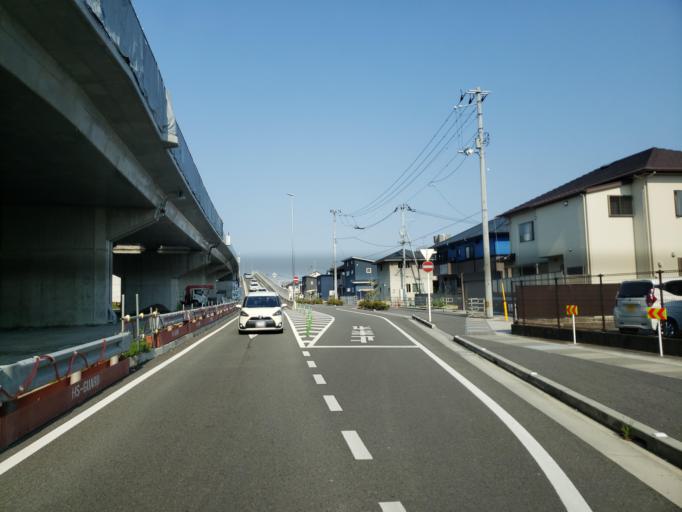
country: JP
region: Ehime
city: Masaki-cho
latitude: 33.8111
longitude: 132.7281
